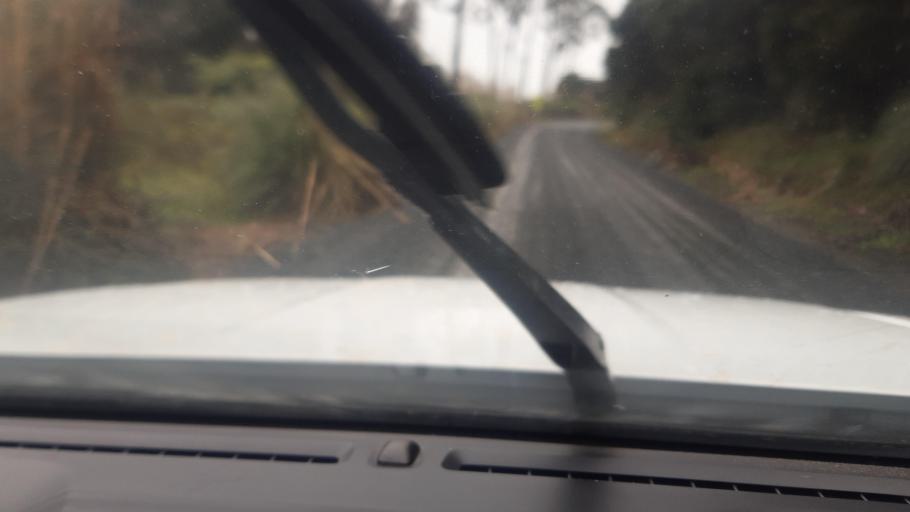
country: NZ
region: Northland
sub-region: Far North District
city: Kaitaia
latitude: -34.9947
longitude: 173.2172
